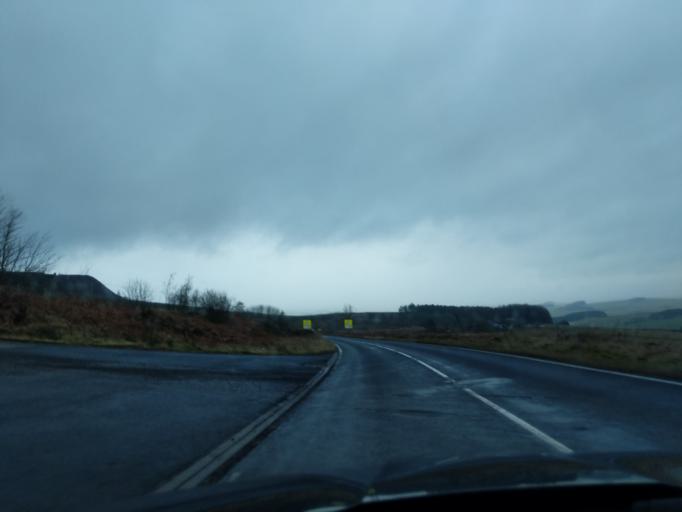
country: GB
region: England
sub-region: Northumberland
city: Otterburn
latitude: 55.2073
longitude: -2.0986
